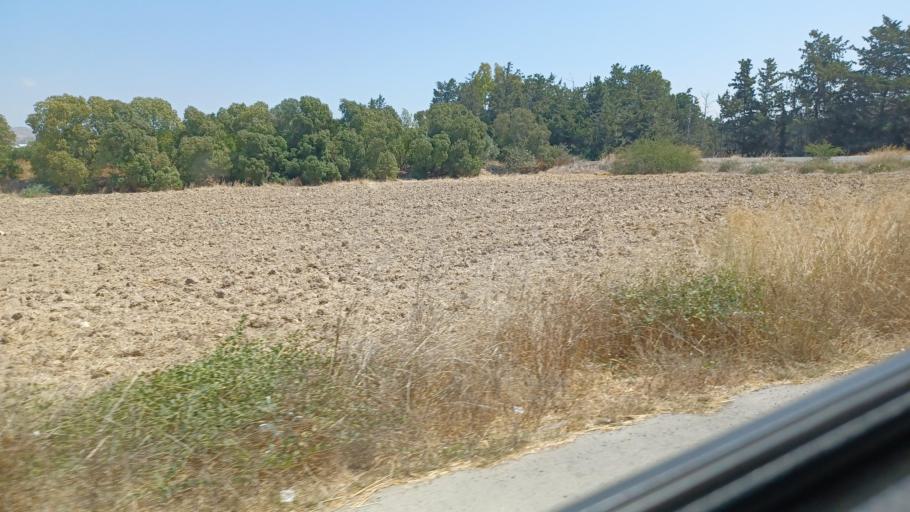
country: CY
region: Pafos
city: Paphos
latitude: 34.7340
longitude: 32.4833
